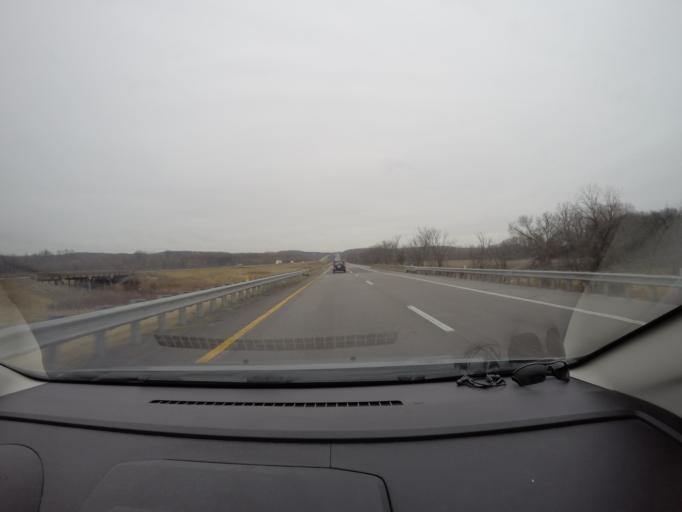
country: US
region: Missouri
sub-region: Montgomery County
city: Montgomery City
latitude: 38.8986
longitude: -91.5911
